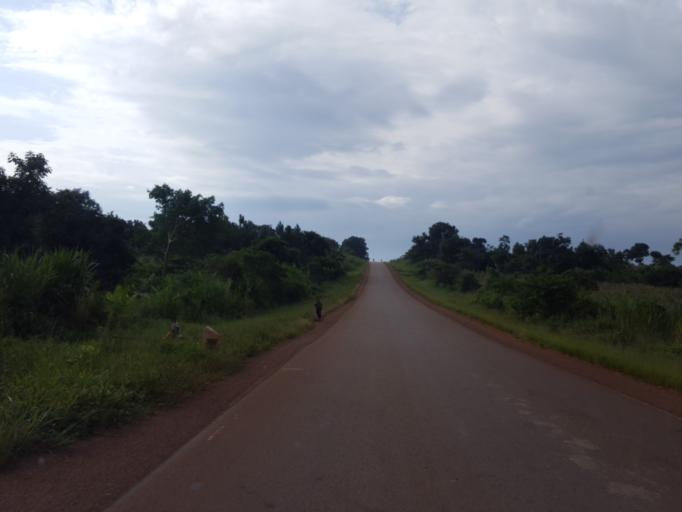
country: UG
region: Western Region
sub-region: Hoima District
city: Hoima
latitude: 1.2492
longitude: 31.5213
